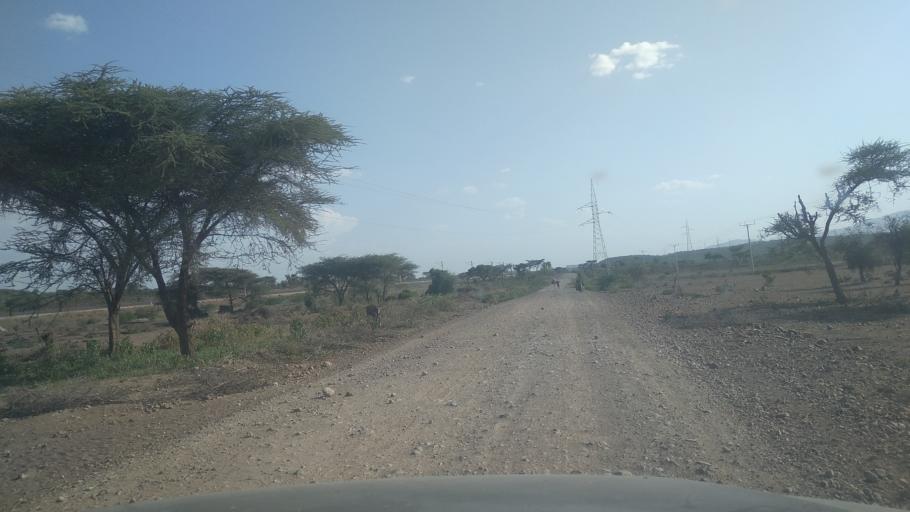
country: ET
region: Oromiya
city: Hirna
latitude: 9.4924
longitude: 41.0255
